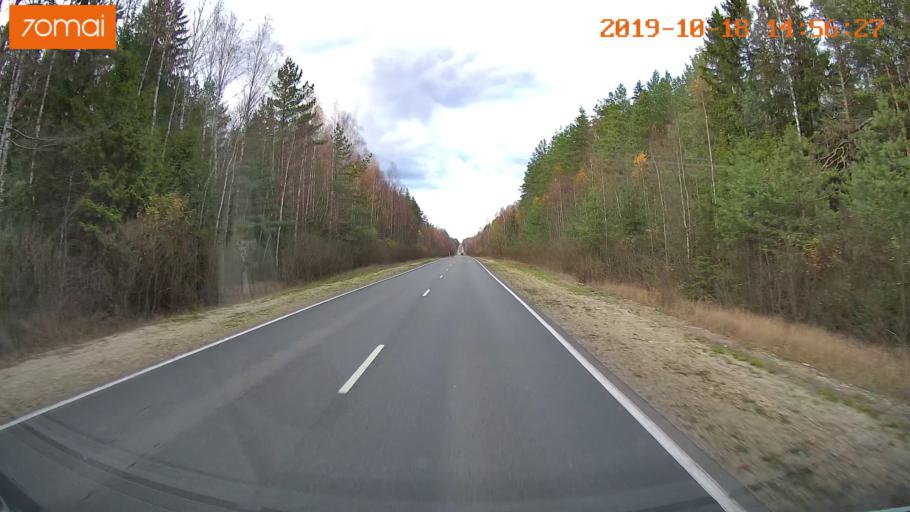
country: RU
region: Vladimir
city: Kurlovo
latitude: 55.4649
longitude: 40.5875
